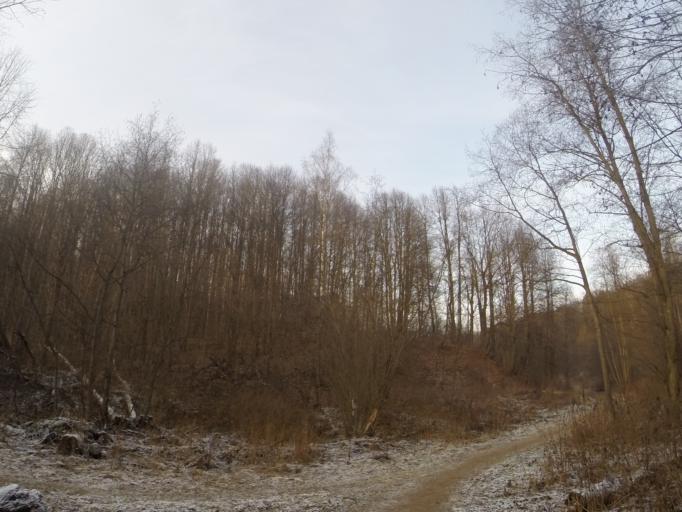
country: RU
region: Moskovskaya
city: Krasnogorsk
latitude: 55.8425
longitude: 37.3010
